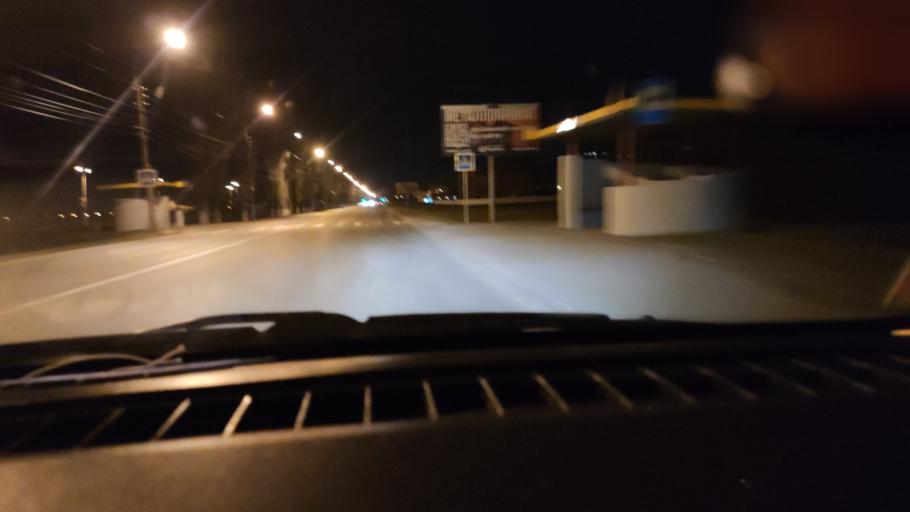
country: RU
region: Saratov
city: Privolzhskiy
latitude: 51.4446
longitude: 46.0733
